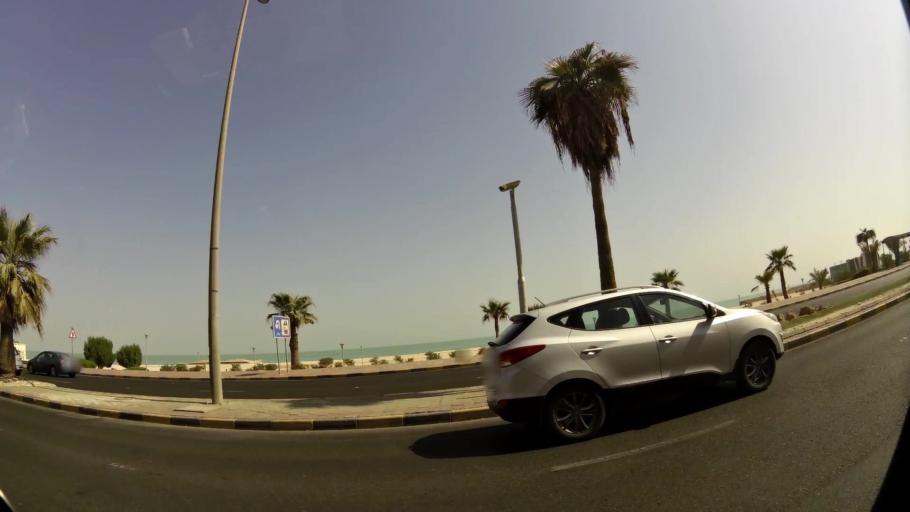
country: KW
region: Muhafazat Hawalli
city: As Salimiyah
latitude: 29.3306
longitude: 48.0918
